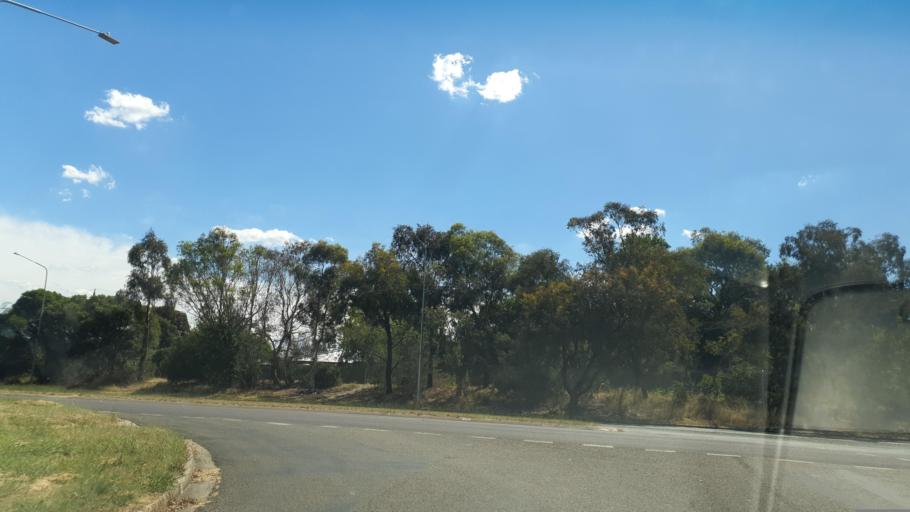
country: AU
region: Australian Capital Territory
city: Belconnen
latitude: -35.2104
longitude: 149.0484
